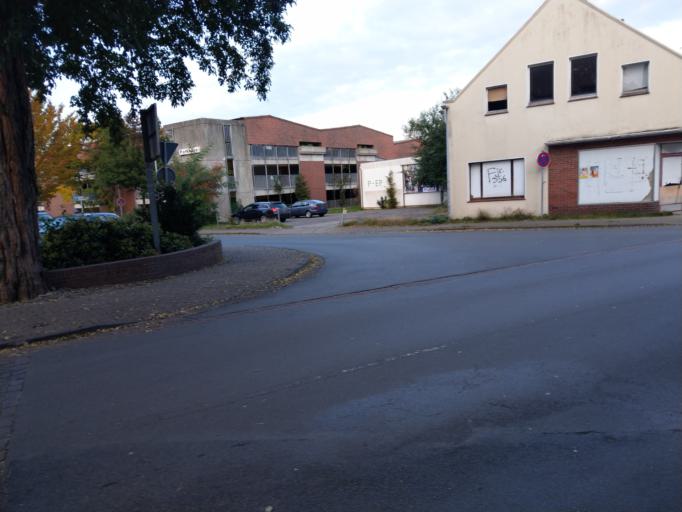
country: DE
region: Lower Saxony
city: Diepholz
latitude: 52.6064
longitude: 8.3708
